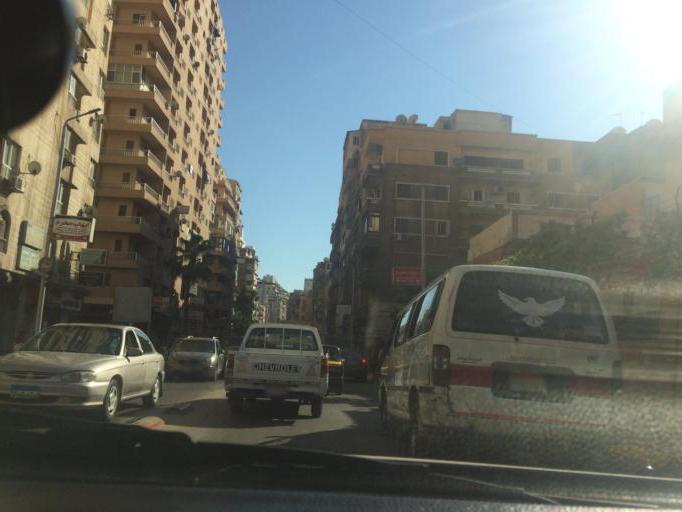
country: EG
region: Alexandria
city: Alexandria
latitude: 31.2427
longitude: 29.9691
